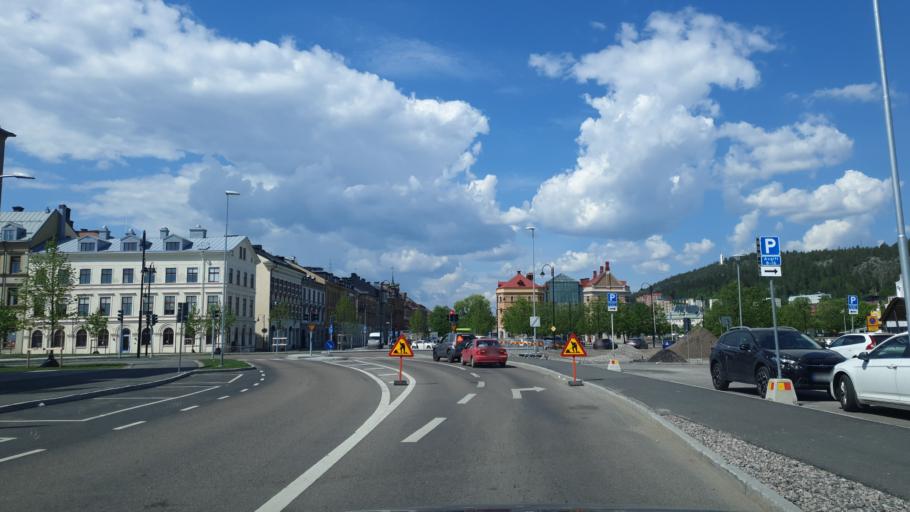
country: SE
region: Vaesternorrland
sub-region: Sundsvalls Kommun
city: Sundsvall
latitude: 62.3908
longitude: 17.3164
